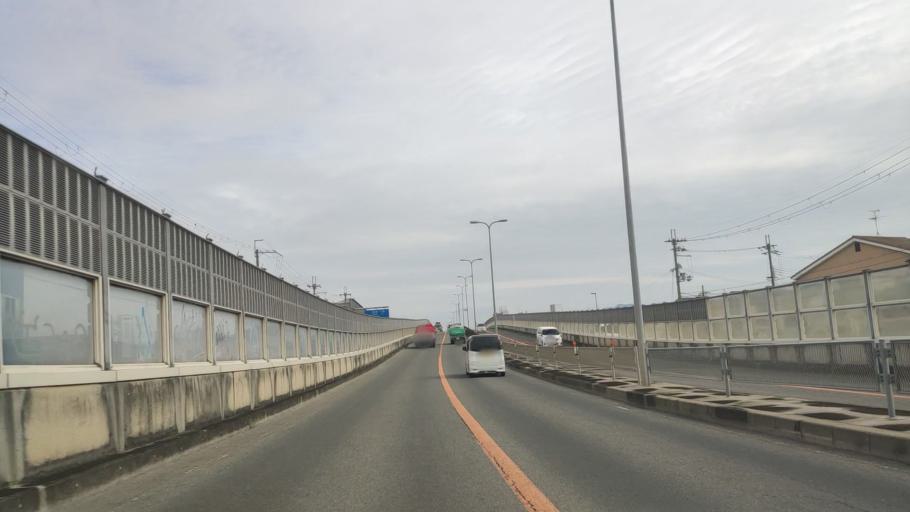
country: JP
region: Osaka
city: Kashihara
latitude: 34.5572
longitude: 135.5988
